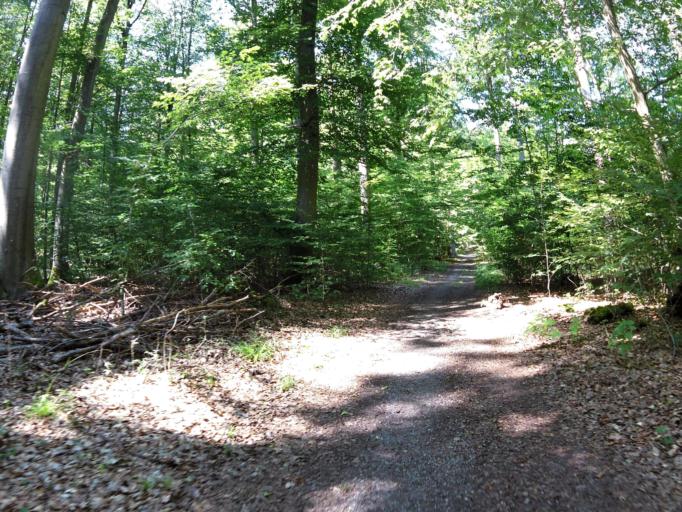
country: DE
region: Bavaria
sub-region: Regierungsbezirk Unterfranken
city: Gadheim
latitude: 49.8513
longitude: 9.8939
